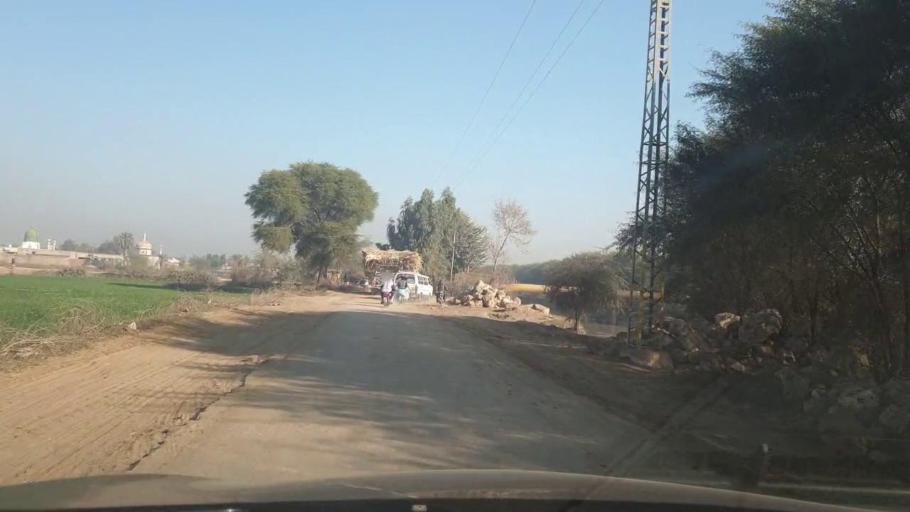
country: PK
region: Sindh
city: Mirpur Mathelo
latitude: 28.0745
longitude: 69.4681
